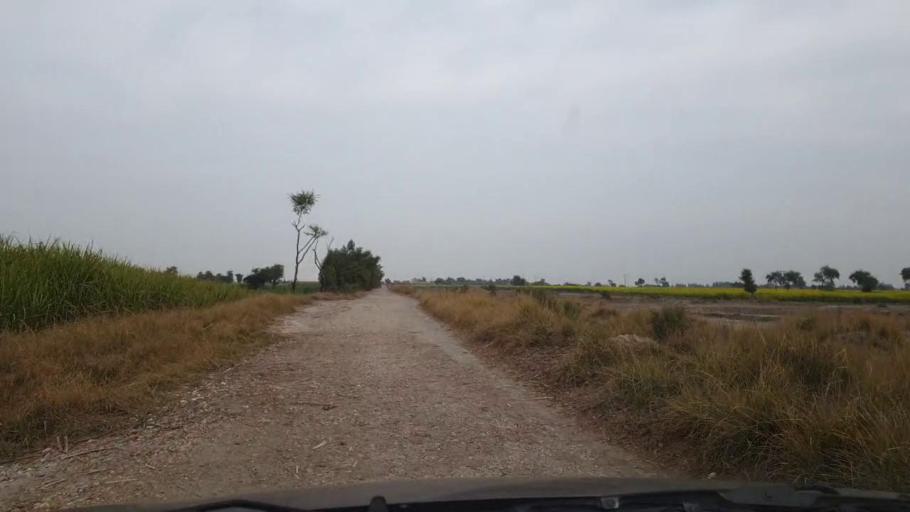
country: PK
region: Sindh
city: Sanghar
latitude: 26.1123
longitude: 68.8963
